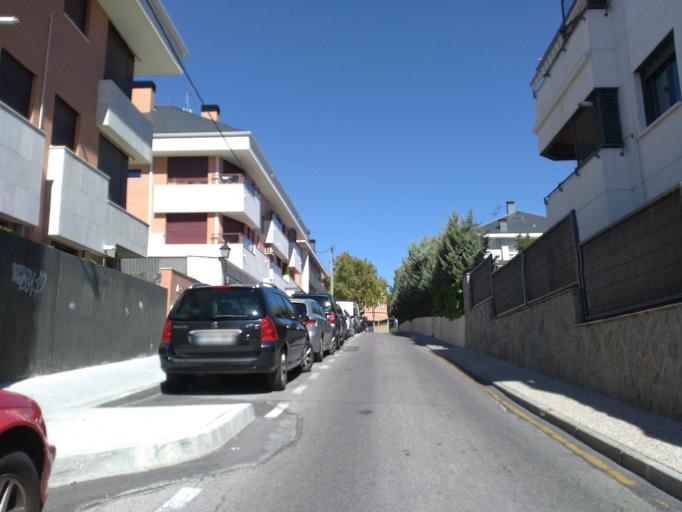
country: ES
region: Madrid
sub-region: Provincia de Madrid
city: Torrelodones
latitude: 40.5784
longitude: -3.9300
